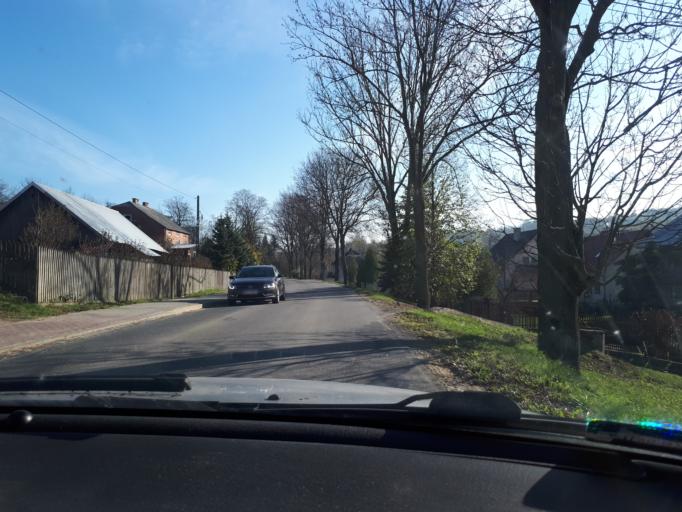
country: PL
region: Subcarpathian Voivodeship
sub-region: Powiat debicki
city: Debica
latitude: 49.9997
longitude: 21.4142
